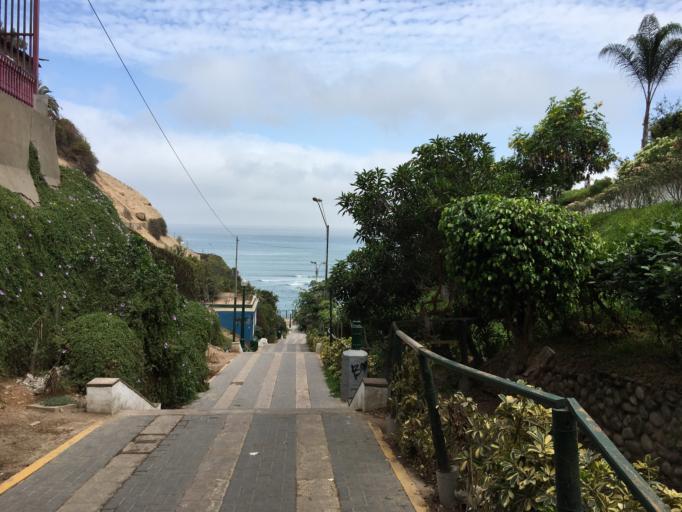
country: PE
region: Lima
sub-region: Lima
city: Surco
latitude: -12.1500
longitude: -77.0234
